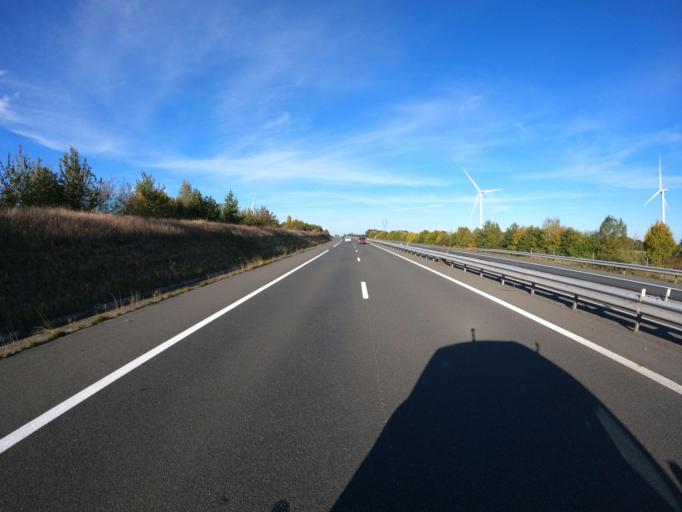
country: FR
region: Pays de la Loire
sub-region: Departement de Maine-et-Loire
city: Saint-Lambert-du-Lattay
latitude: 47.2484
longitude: -0.6266
